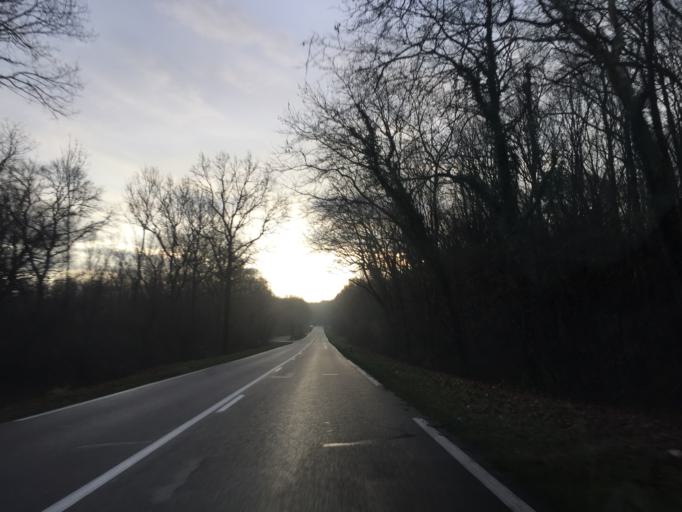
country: FR
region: Franche-Comte
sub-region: Departement du Jura
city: Choisey
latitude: 47.0070
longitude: 5.4985
